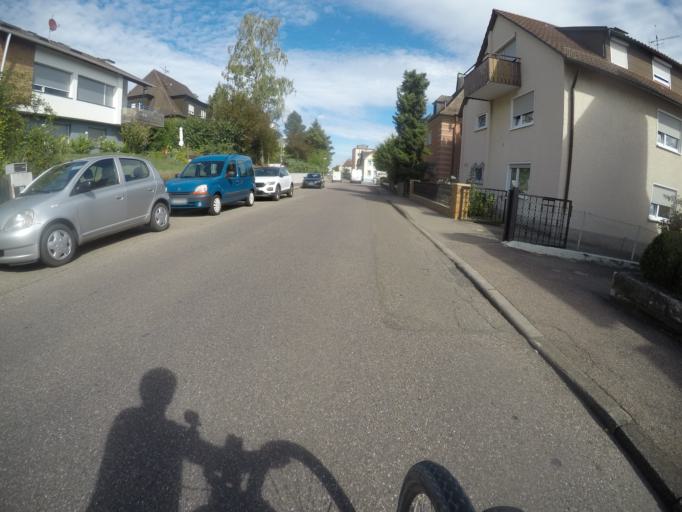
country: DE
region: Baden-Wuerttemberg
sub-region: Regierungsbezirk Stuttgart
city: Asperg
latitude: 48.9076
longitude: 9.1407
